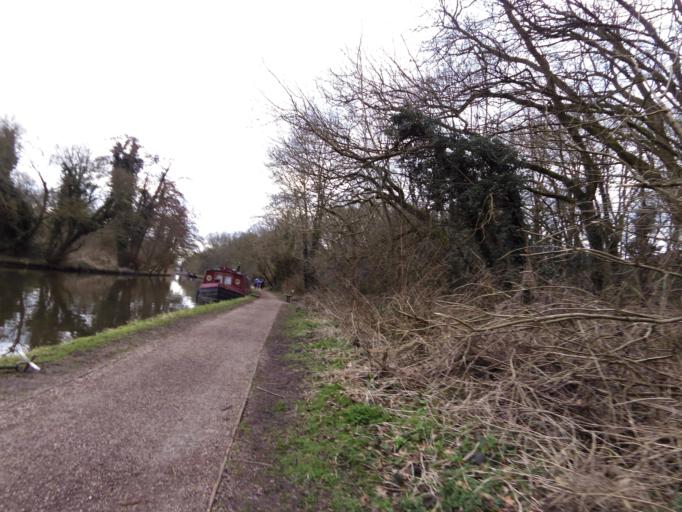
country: GB
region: England
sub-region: Hertfordshire
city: Watford
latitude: 51.6620
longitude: -0.4278
